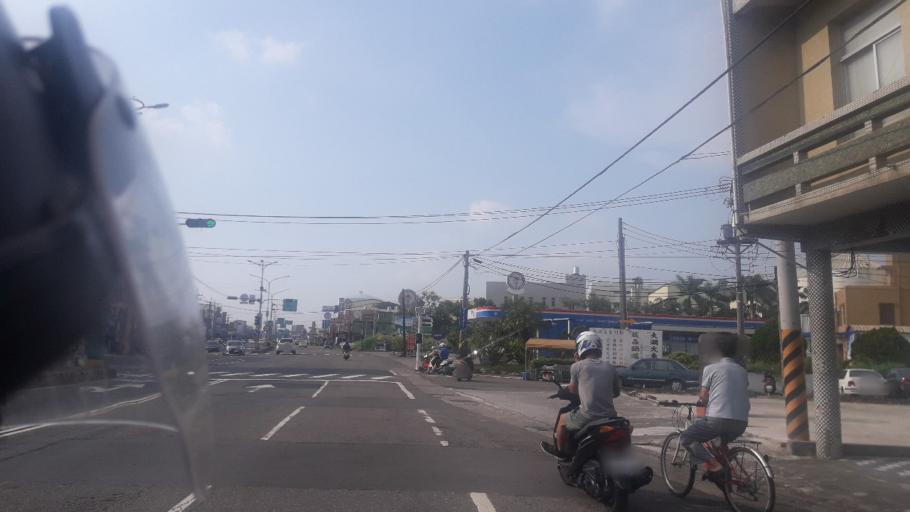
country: TW
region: Taiwan
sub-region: Tainan
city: Tainan
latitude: 22.8778
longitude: 120.2523
